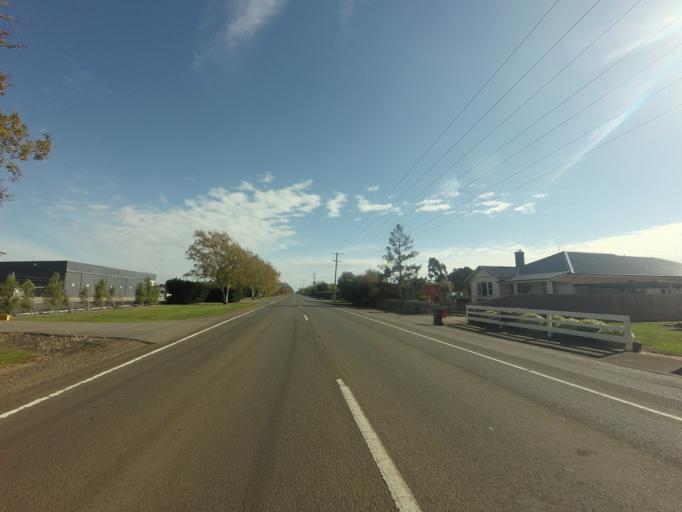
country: AU
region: Tasmania
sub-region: Meander Valley
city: Westbury
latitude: -41.5261
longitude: 146.8906
